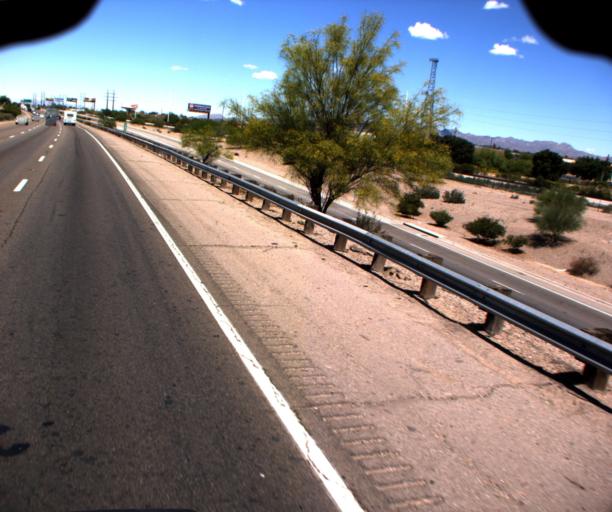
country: US
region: Arizona
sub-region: Pima County
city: Flowing Wells
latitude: 32.3235
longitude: -111.0516
